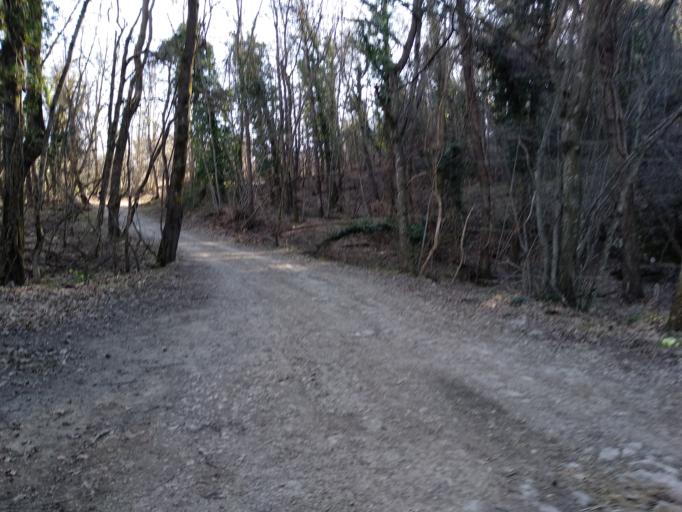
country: IT
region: Emilia-Romagna
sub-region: Provincia di Reggio Emilia
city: Castelnovo ne'Monti
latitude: 44.4204
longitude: 10.4177
